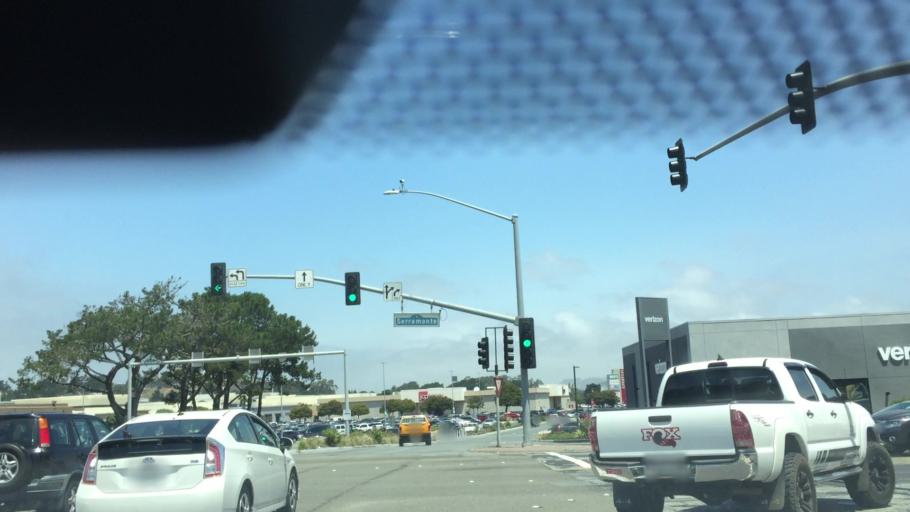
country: US
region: California
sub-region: San Mateo County
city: Colma
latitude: 37.6689
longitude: -122.4688
